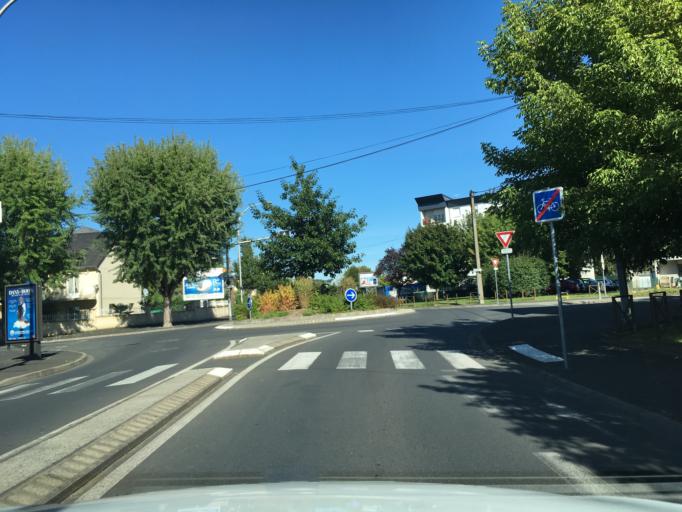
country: FR
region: Limousin
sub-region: Departement de la Correze
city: Brive-la-Gaillarde
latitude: 45.1578
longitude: 1.4936
